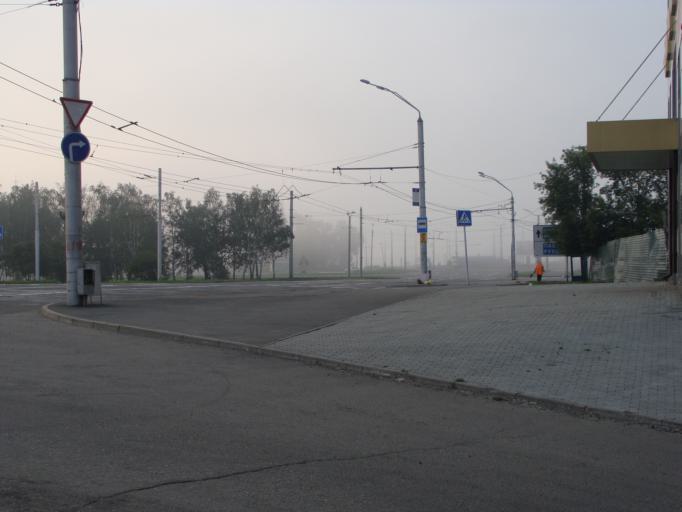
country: RU
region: Altai Krai
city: Zaton
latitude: 53.3285
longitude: 83.7974
